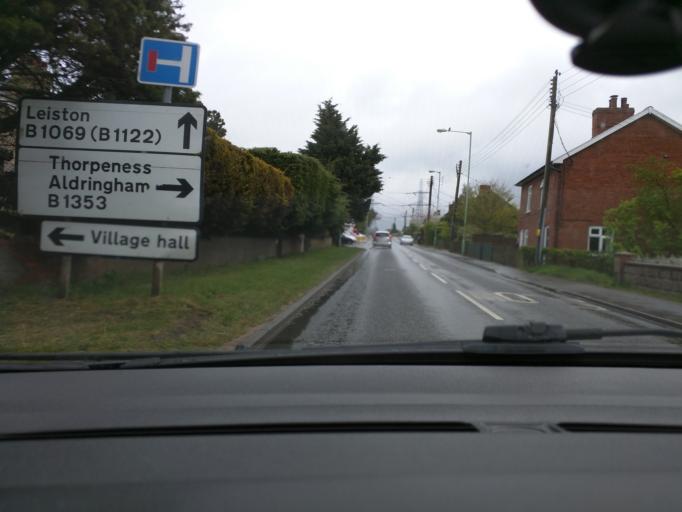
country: GB
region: England
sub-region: Suffolk
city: Leiston
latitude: 52.1932
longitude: 1.5617
